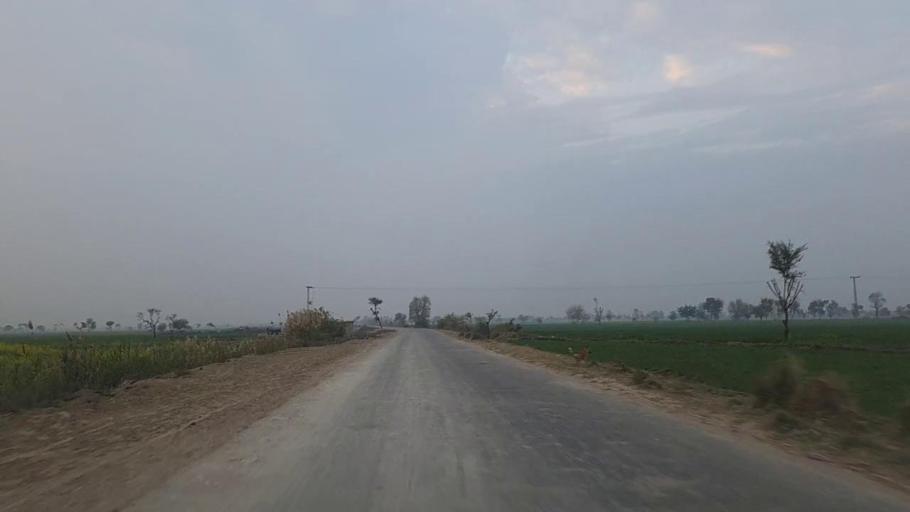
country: PK
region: Sindh
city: Jam Sahib
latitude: 26.3182
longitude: 68.5643
